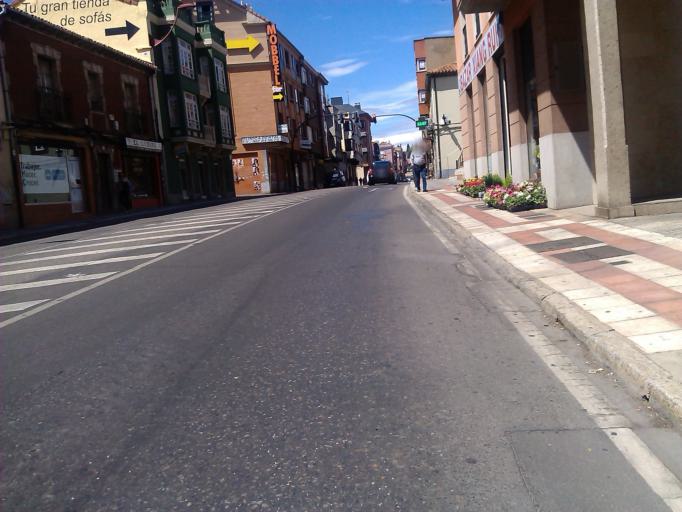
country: ES
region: Castille and Leon
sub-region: Provincia de Leon
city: San Andres del Rabanedo
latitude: 42.5965
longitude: -5.6058
